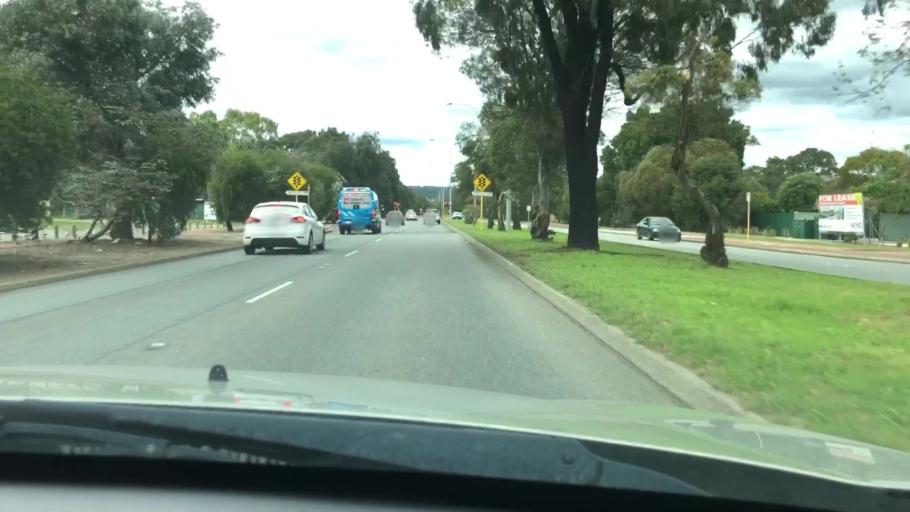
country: AU
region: Western Australia
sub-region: Armadale
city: Seville Grove
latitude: -32.1470
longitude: 115.9890
